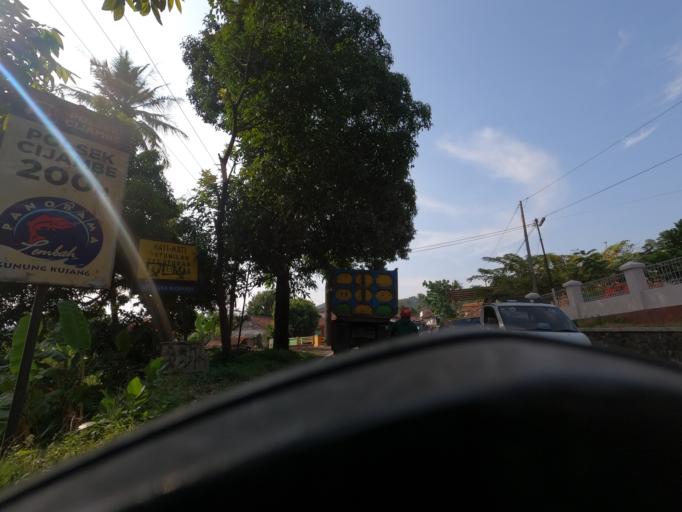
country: ID
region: West Java
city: Lembang
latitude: -6.6413
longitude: 107.7244
